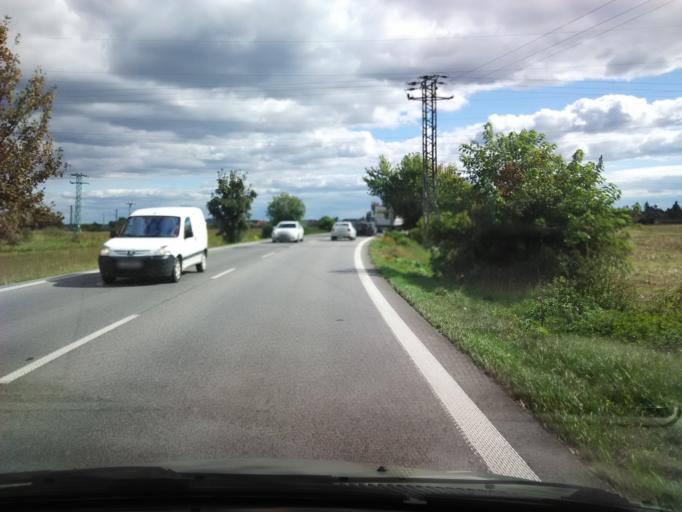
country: SK
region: Nitriansky
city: Levice
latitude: 48.1994
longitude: 18.5349
